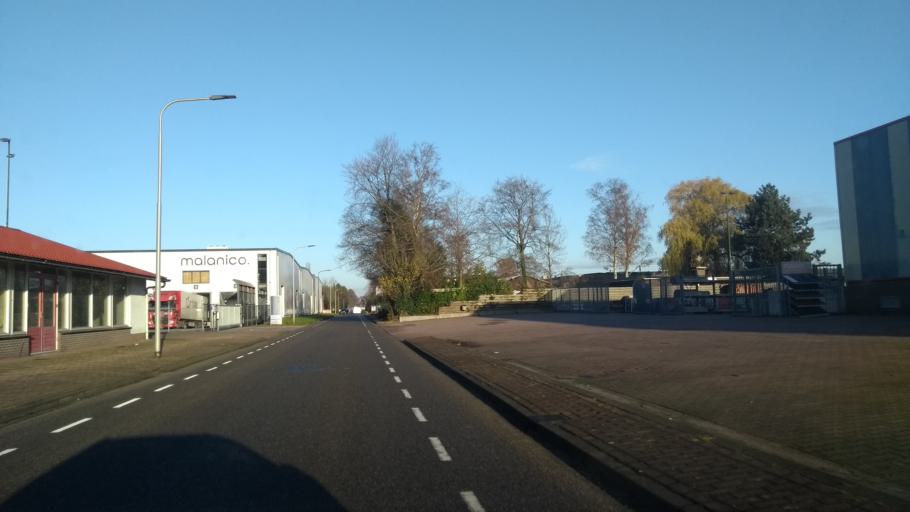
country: NL
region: Overijssel
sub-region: Gemeente Dalfsen
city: Dalfsen
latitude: 52.5927
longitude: 6.2863
